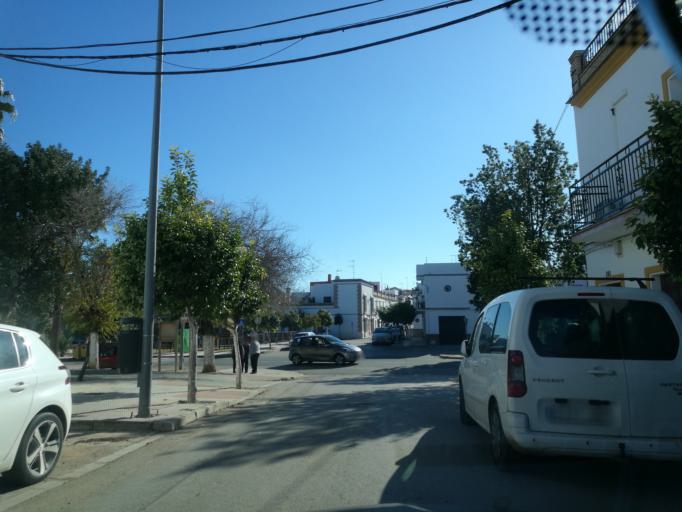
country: ES
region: Andalusia
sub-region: Provincia de Sevilla
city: La Campana
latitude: 37.5725
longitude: -5.4288
